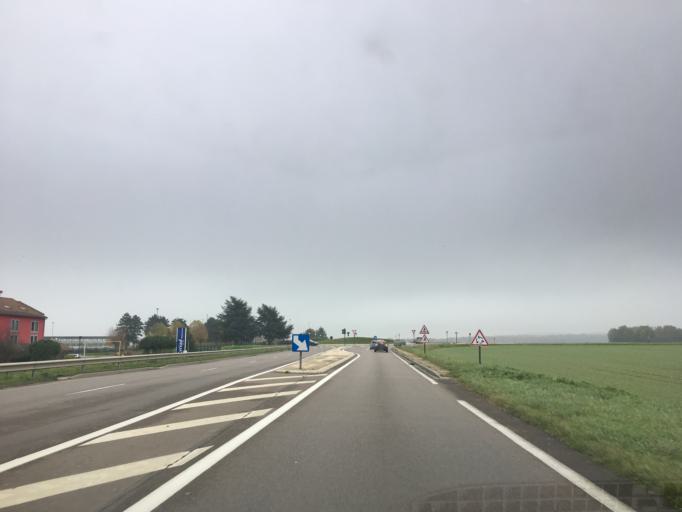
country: FR
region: Ile-de-France
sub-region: Departement de Seine-et-Marne
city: Cannes-Ecluse
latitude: 48.3580
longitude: 2.9819
